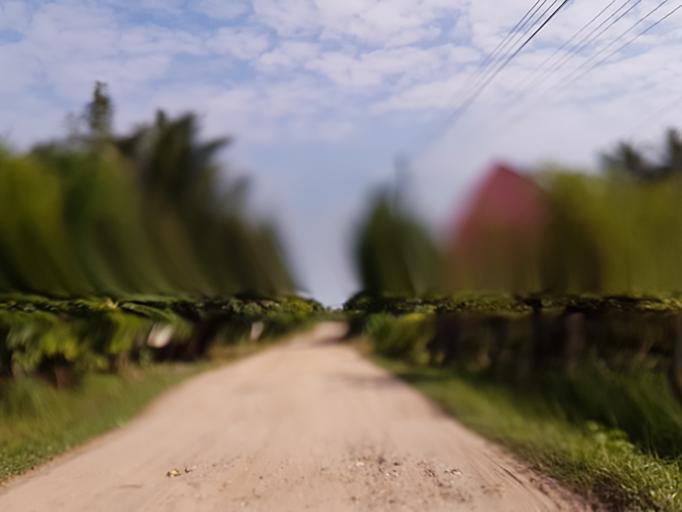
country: TH
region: Nong Khai
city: Tha Bo
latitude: 17.8665
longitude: 102.6074
